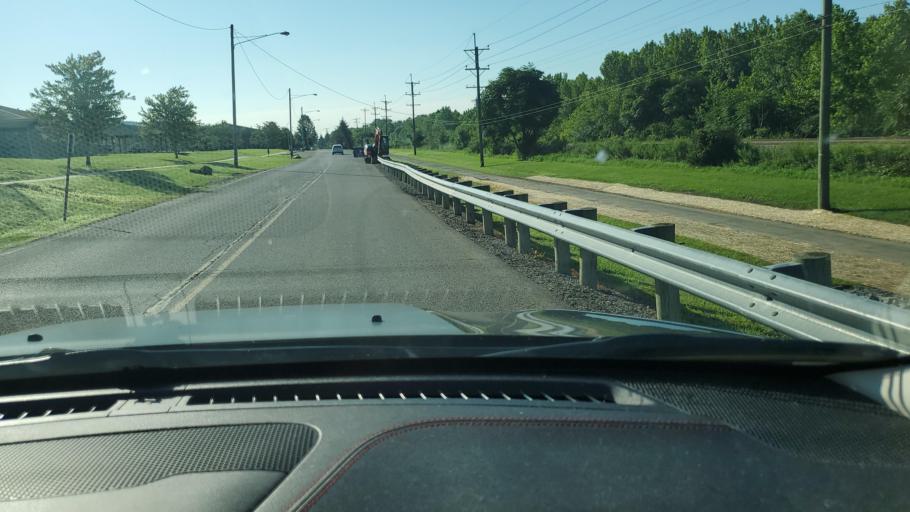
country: US
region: Ohio
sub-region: Mahoning County
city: Lowellville
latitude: 41.0455
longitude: -80.5566
